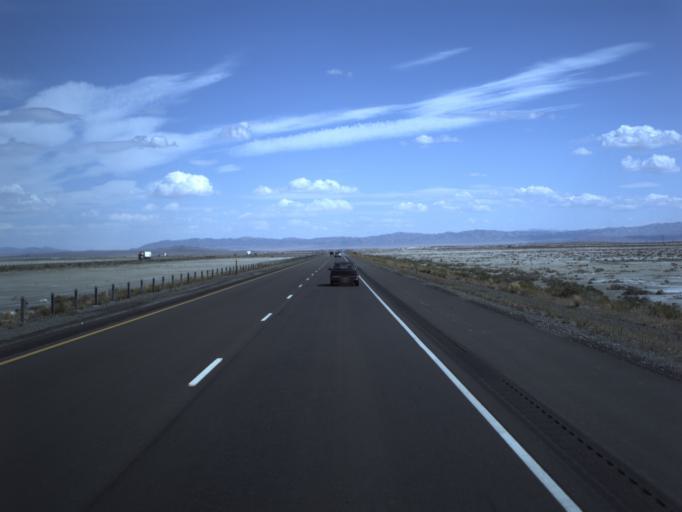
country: US
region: Utah
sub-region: Tooele County
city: Wendover
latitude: 40.7274
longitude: -113.3208
